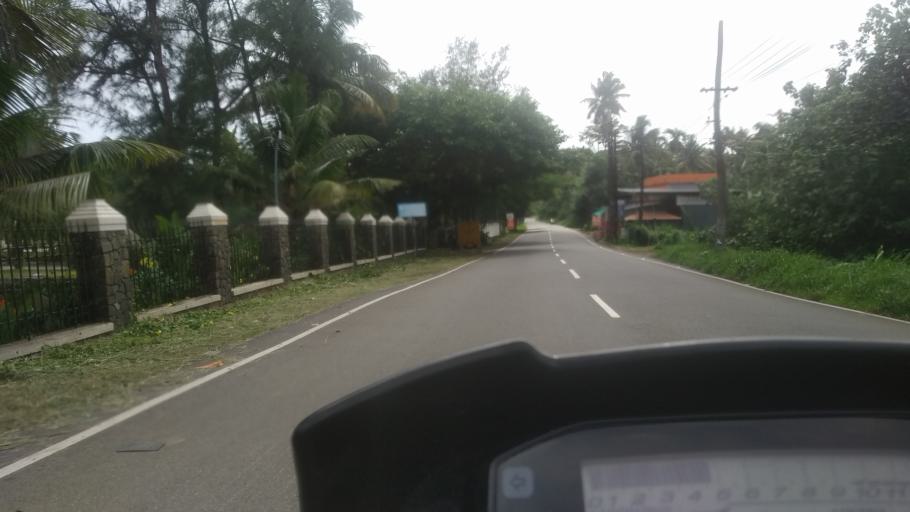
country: IN
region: Kerala
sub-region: Ernakulam
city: Elur
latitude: 10.1443
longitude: 76.2607
